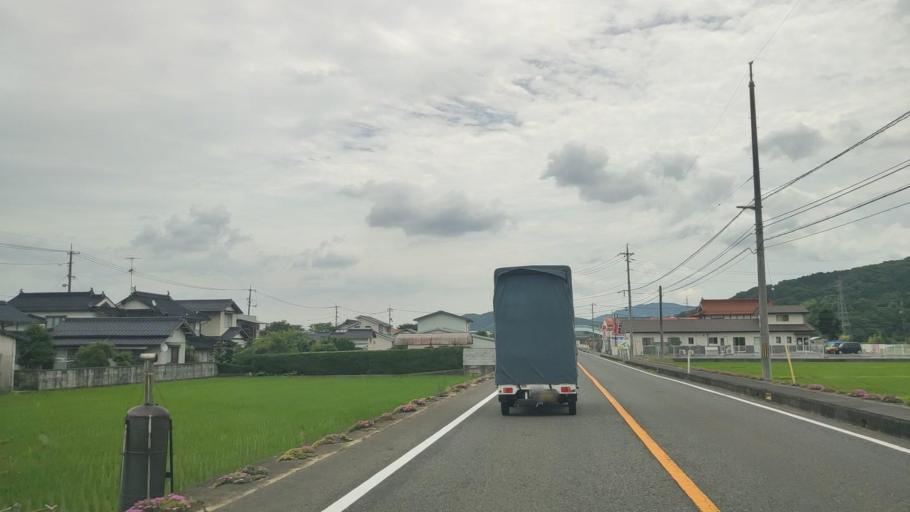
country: JP
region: Okayama
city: Tsuyama
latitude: 35.0548
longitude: 133.9153
